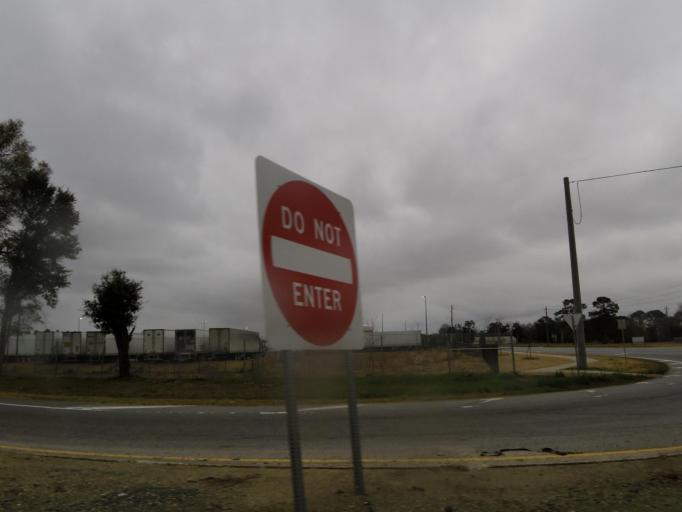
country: US
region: Georgia
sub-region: Dougherty County
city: Albany
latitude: 31.5804
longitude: -84.1099
